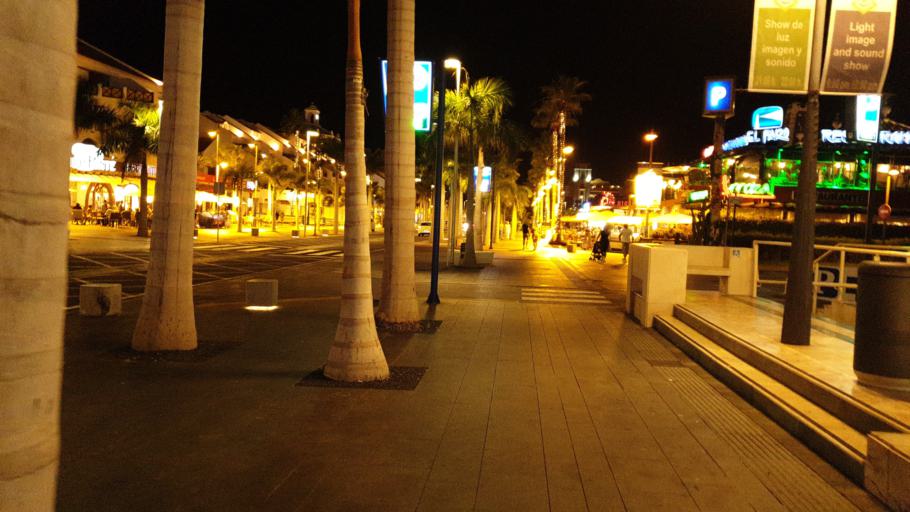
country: ES
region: Canary Islands
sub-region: Provincia de Santa Cruz de Tenerife
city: Playa de las Americas
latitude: 28.0552
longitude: -16.7316
